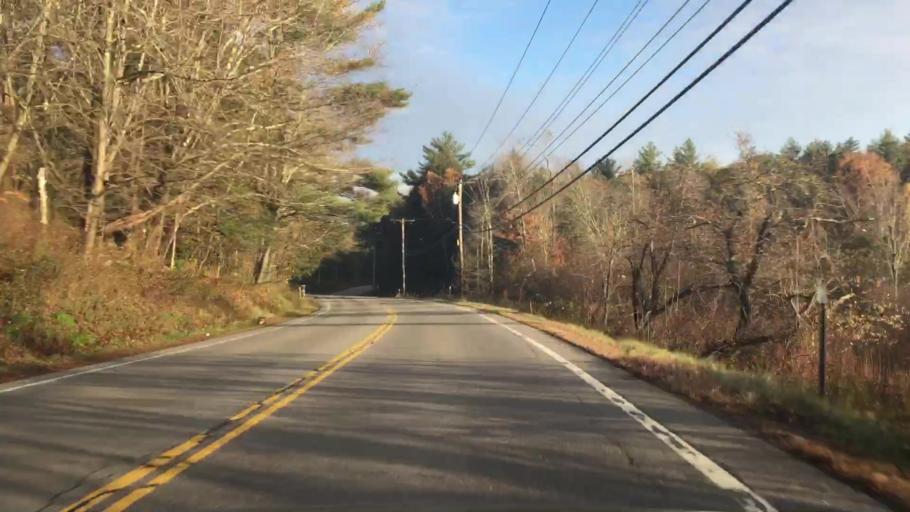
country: US
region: New Hampshire
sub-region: Cheshire County
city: Keene
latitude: 43.0079
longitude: -72.2612
